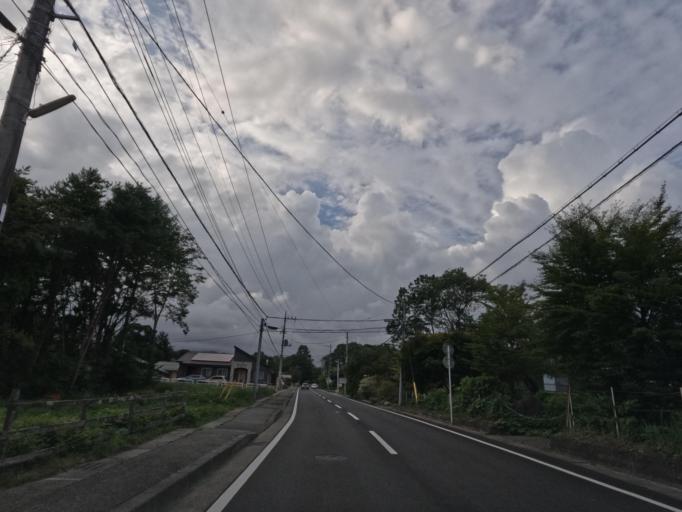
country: JP
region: Yamanashi
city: Nirasaki
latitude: 35.8883
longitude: 138.4112
